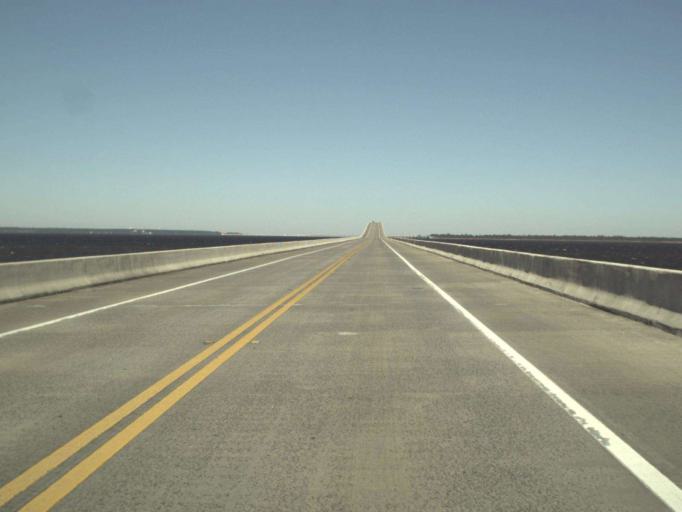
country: US
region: Florida
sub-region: Santa Rosa County
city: Oriole Beach
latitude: 30.4066
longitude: -87.0828
